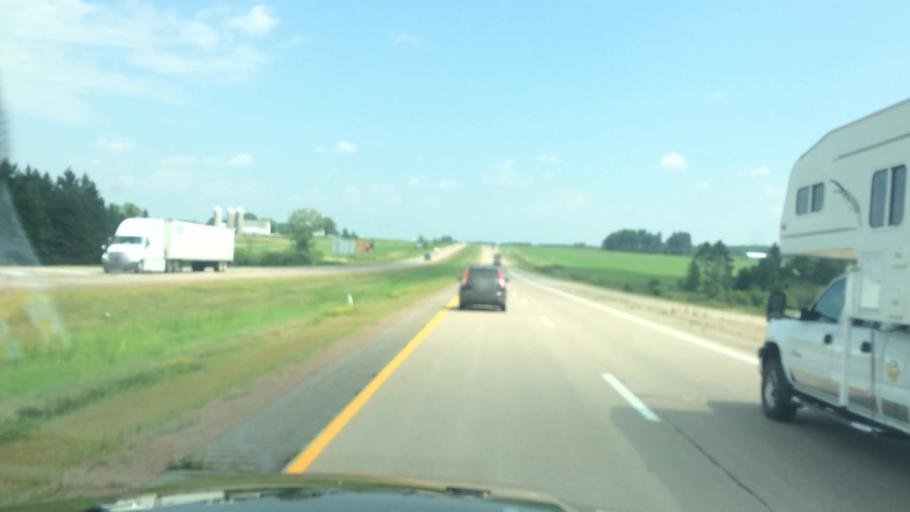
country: US
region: Wisconsin
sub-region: Marathon County
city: Athens
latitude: 44.9450
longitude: -90.0758
